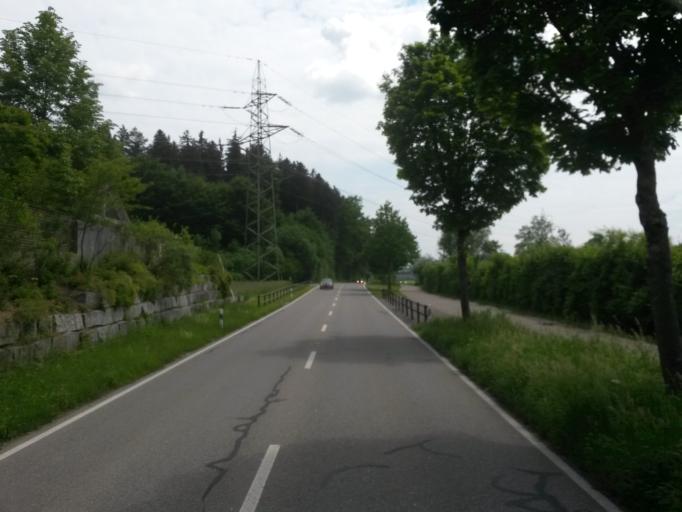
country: CH
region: Zurich
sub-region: Bezirk Pfaeffikon
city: Illnau / Unter-Illnau
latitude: 47.4029
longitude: 8.7304
